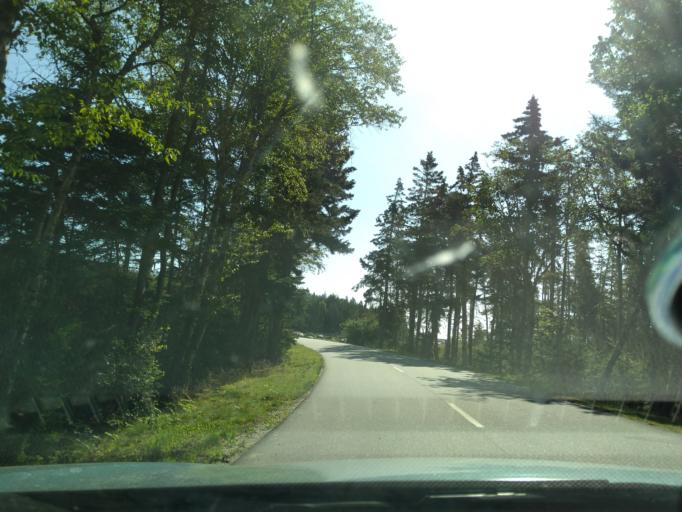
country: US
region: Maine
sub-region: Hancock County
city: Gouldsboro
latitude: 44.3385
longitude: -68.0548
